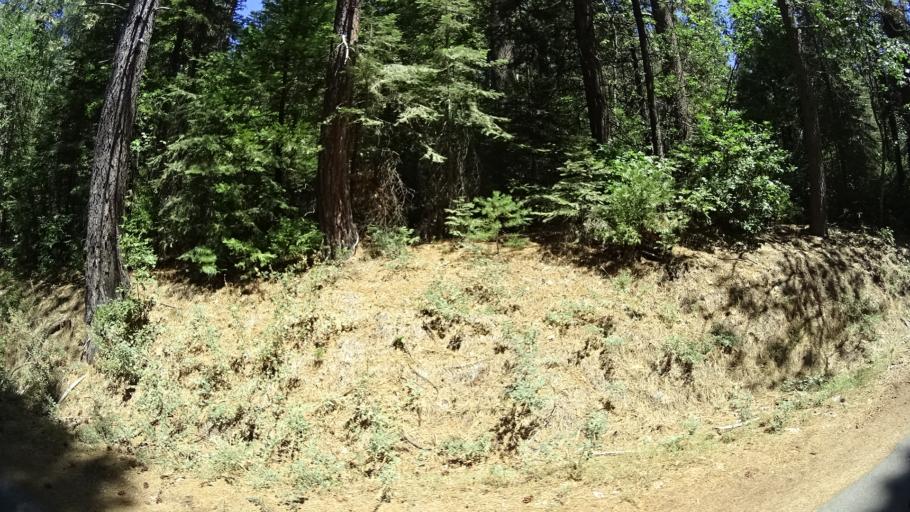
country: US
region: California
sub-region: Calaveras County
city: Arnold
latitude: 38.2374
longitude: -120.3178
